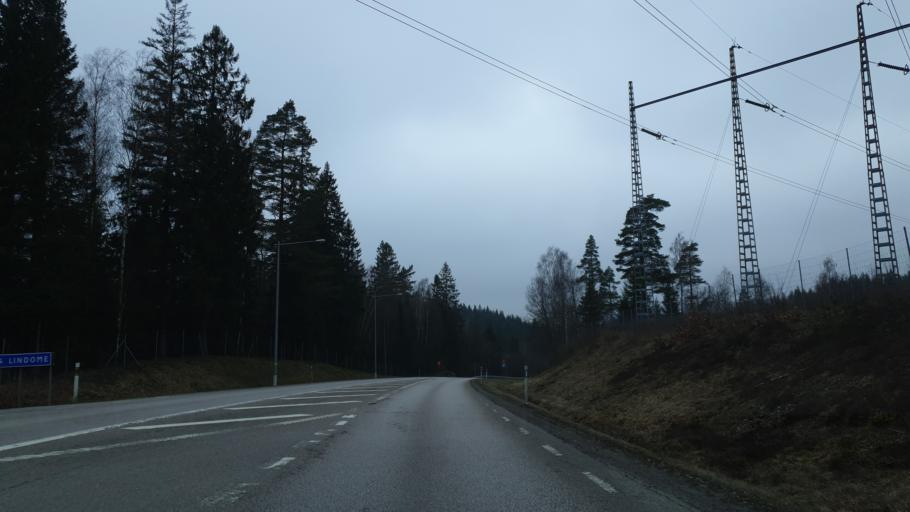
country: SE
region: Vaestra Goetaland
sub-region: Harryda Kommun
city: Hindas
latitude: 57.6219
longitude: 12.4218
